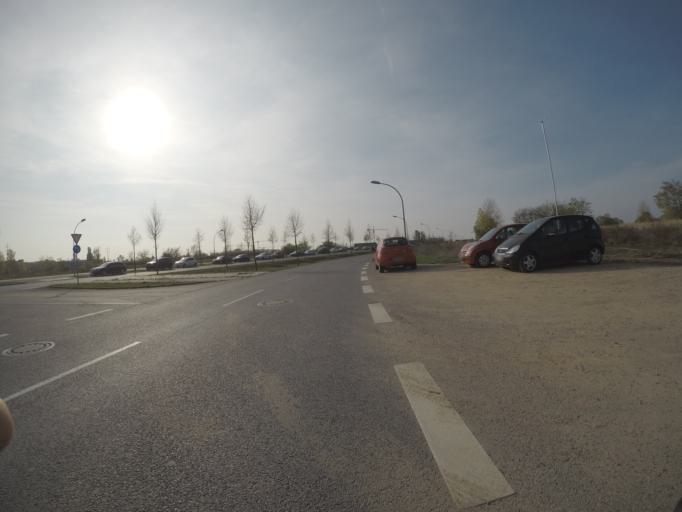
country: DE
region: Brandenburg
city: Schonefeld
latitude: 52.3935
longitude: 13.5103
